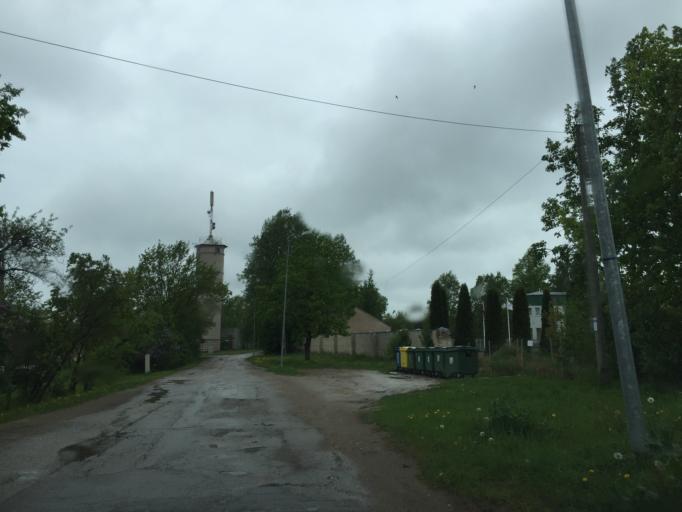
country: LV
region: Lielvarde
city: Lielvarde
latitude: 56.7223
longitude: 24.7901
